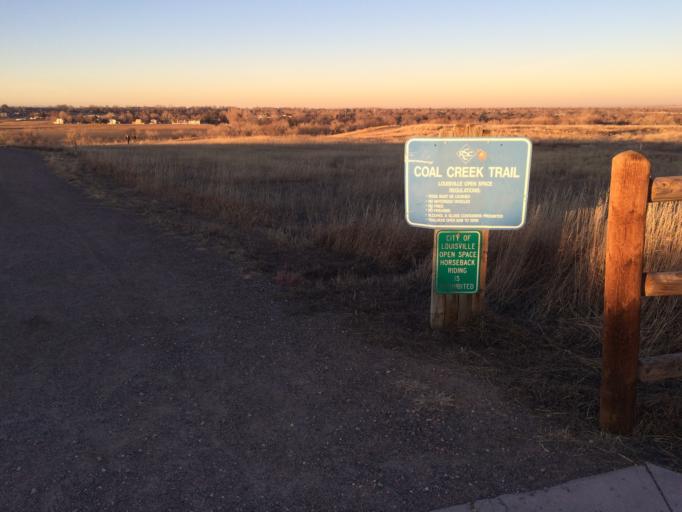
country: US
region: Colorado
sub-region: Boulder County
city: Louisville
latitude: 39.9734
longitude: -105.1150
